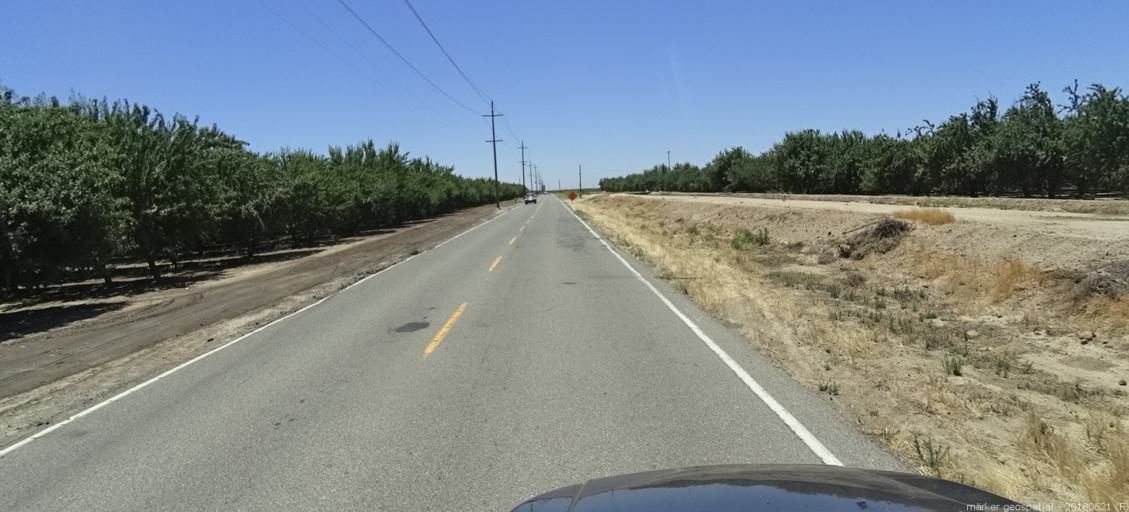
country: US
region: California
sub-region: Fresno County
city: Biola
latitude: 36.8653
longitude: -119.9113
